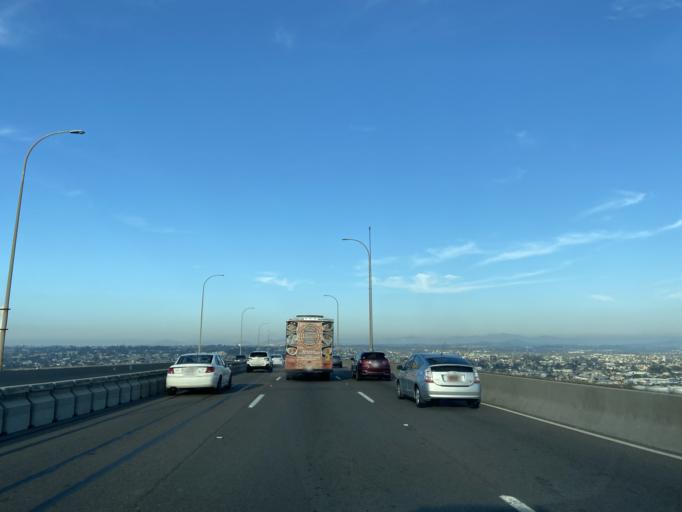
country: US
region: California
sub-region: San Diego County
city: San Diego
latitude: 32.6915
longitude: -117.1511
